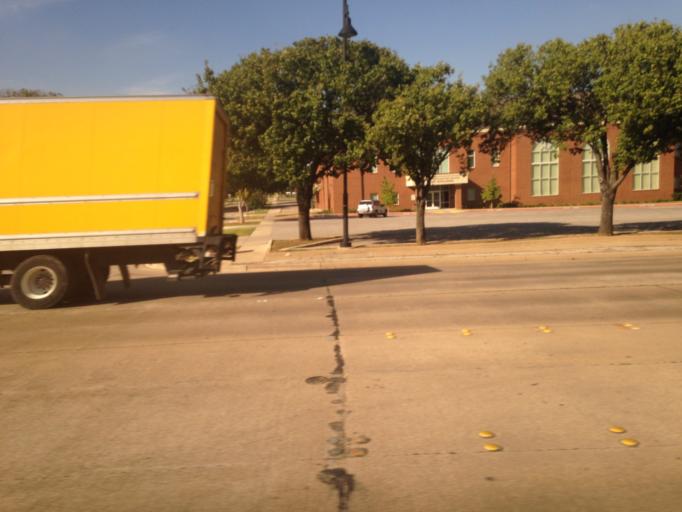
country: US
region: Texas
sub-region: Tarrant County
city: Fort Worth
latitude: 32.7059
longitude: -97.3346
